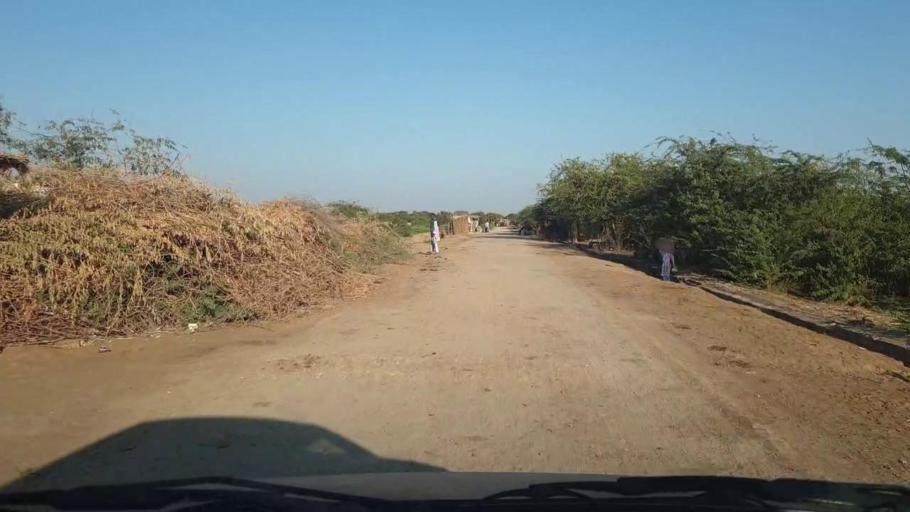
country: PK
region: Sindh
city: Samaro
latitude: 25.3272
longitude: 69.3216
